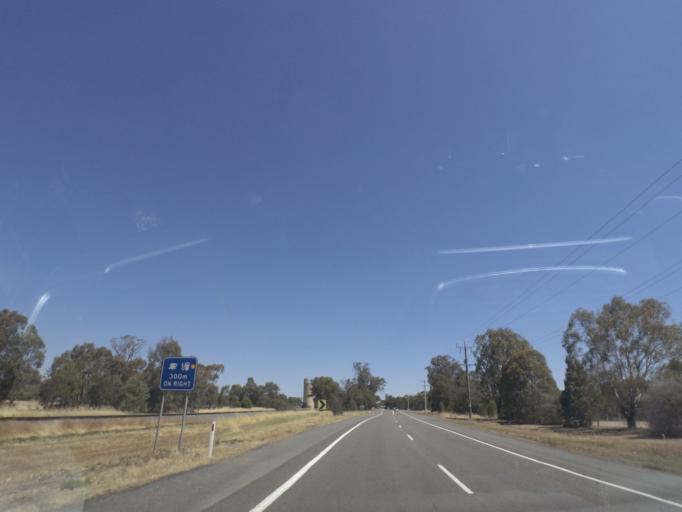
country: AU
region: Victoria
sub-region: Greater Shepparton
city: Shepparton
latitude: -36.2340
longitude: 145.4318
